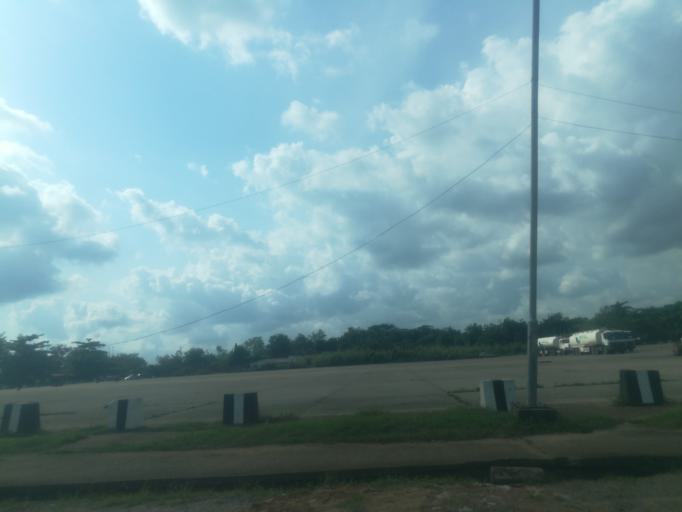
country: NG
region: Oyo
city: Ibadan
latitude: 7.3912
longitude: 3.8189
